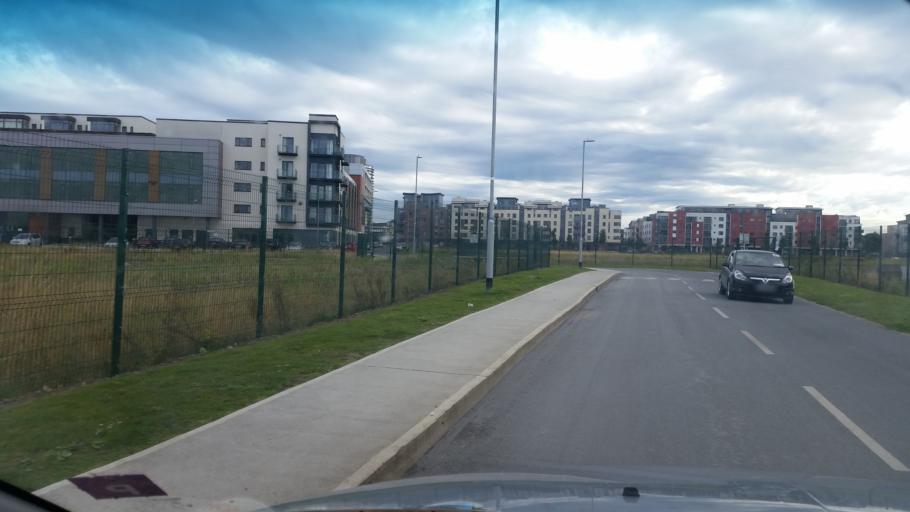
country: IE
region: Leinster
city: Donaghmede
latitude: 53.4053
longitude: -6.1516
